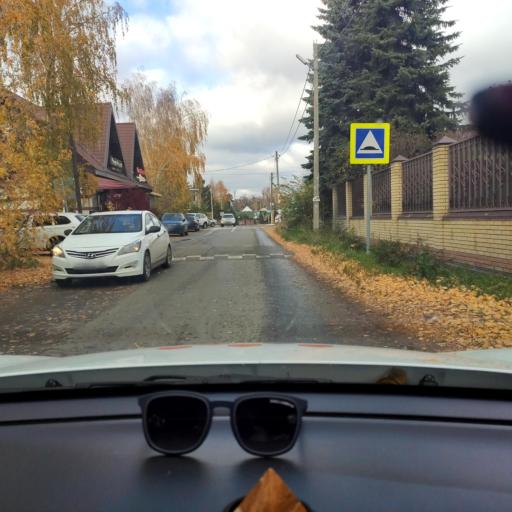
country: RU
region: Tatarstan
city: Verkhniy Uslon
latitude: 55.6209
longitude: 49.0143
